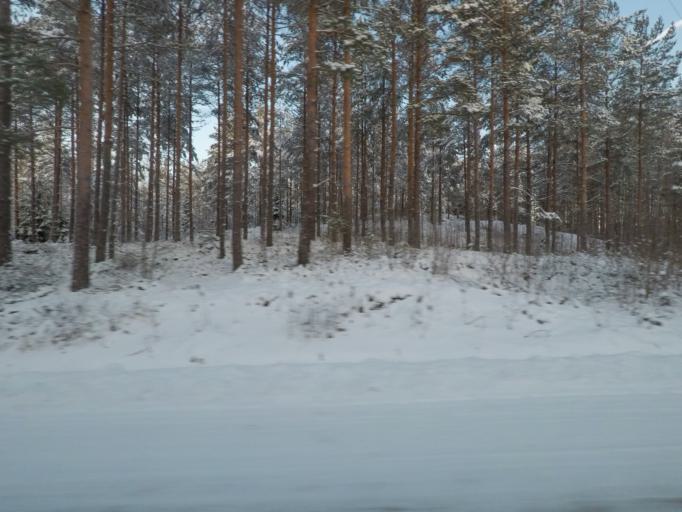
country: FI
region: Varsinais-Suomi
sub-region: Salo
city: Suomusjaervi
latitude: 60.2864
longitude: 23.6546
